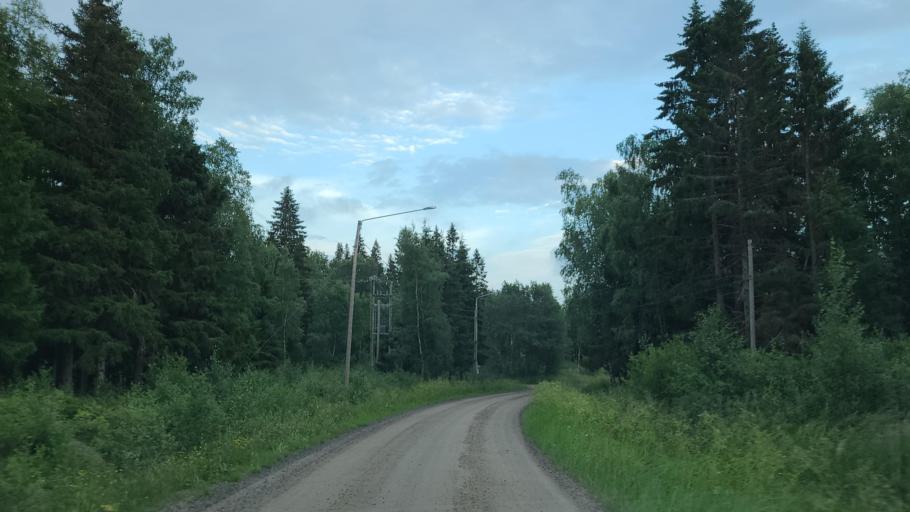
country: FI
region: Ostrobothnia
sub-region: Vaasa
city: Replot
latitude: 63.3142
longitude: 21.1600
